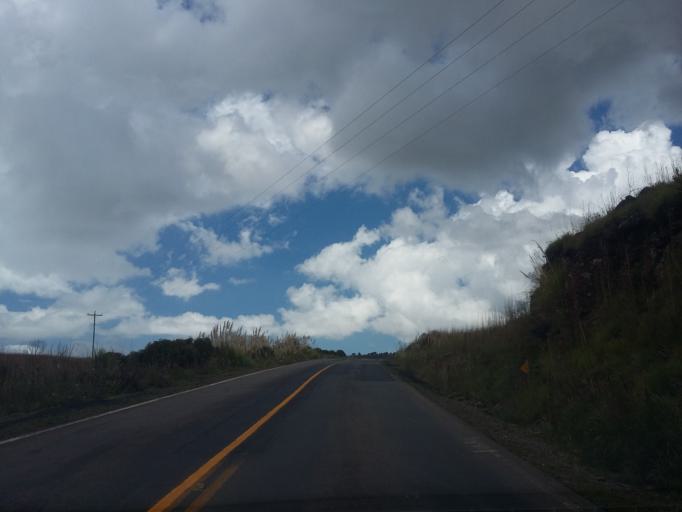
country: BR
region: Santa Catarina
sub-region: Lauro Muller
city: Lauro Muller
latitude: -28.3563
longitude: -49.5907
